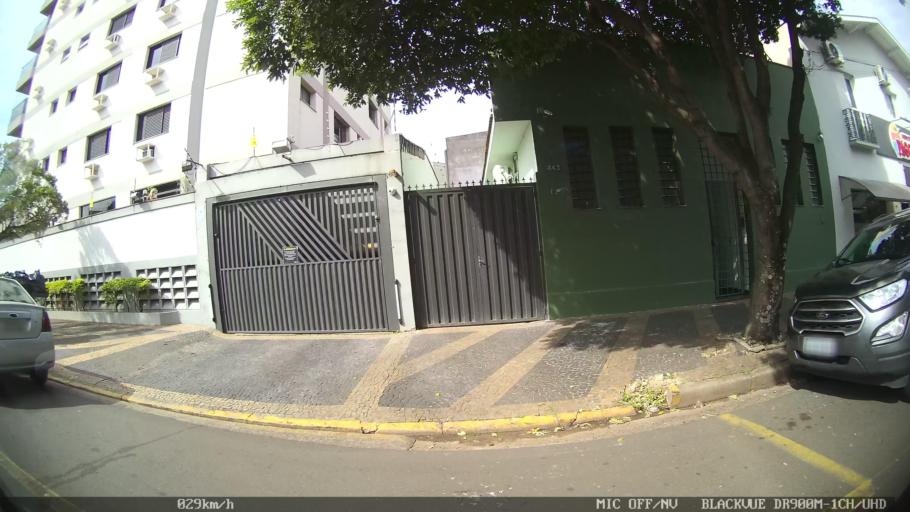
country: BR
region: Sao Paulo
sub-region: Piracicaba
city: Piracicaba
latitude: -22.7135
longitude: -47.6555
